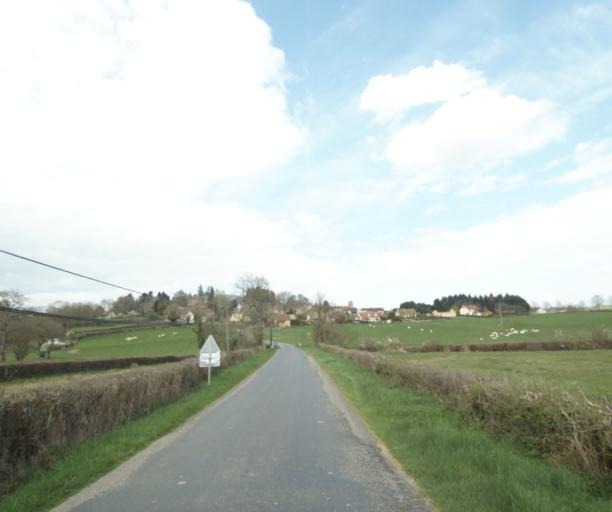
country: FR
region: Bourgogne
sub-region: Departement de Saone-et-Loire
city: Ciry-le-Noble
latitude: 46.5255
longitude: 4.3299
